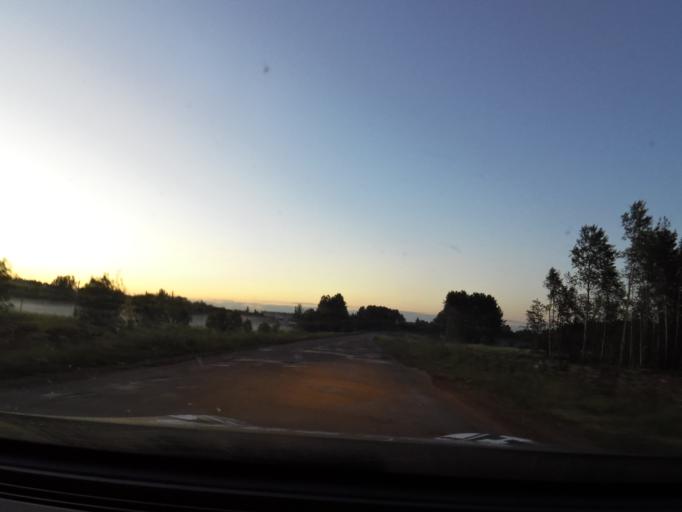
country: RU
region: Vologda
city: Vytegra
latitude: 60.9988
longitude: 36.3790
